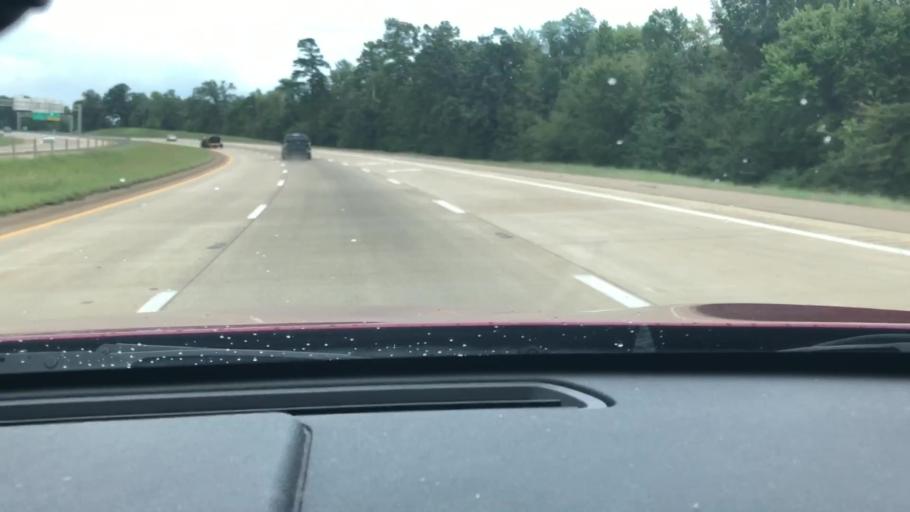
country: US
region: Texas
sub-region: Bowie County
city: Texarkana
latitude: 33.4034
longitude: -94.0055
